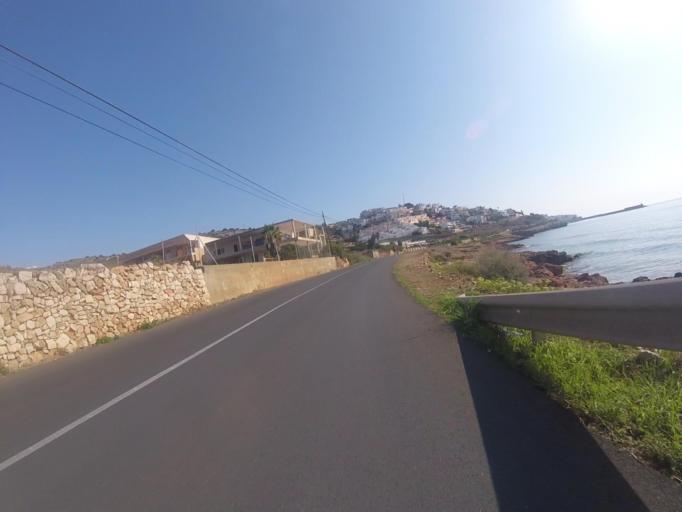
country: ES
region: Valencia
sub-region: Provincia de Castello
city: Peniscola
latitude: 40.3516
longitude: 0.3919
